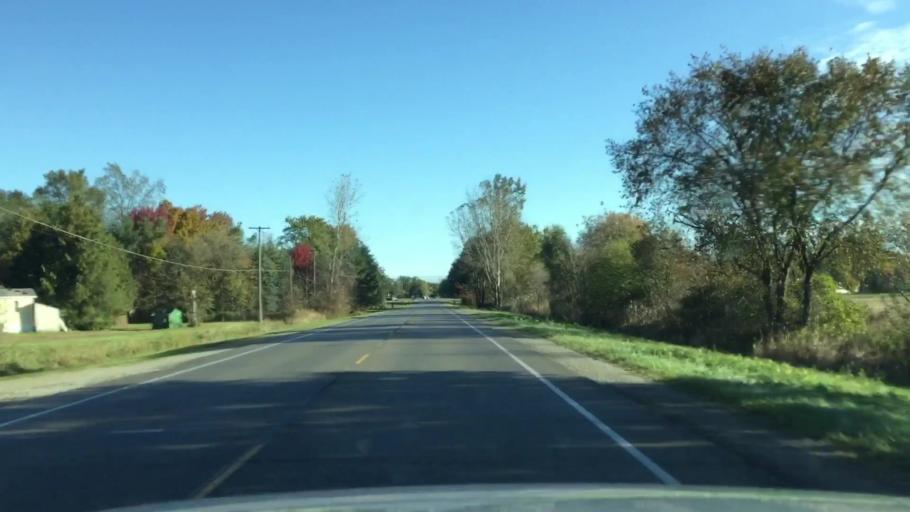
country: US
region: Michigan
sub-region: Shiawassee County
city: Durand
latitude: 42.9465
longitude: -83.9334
